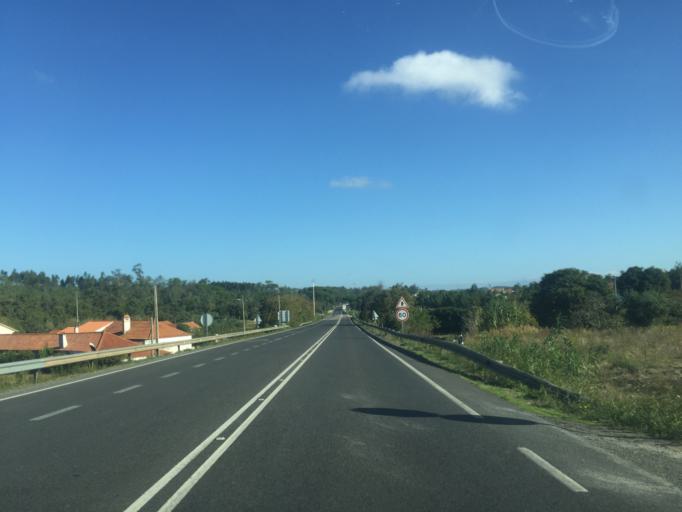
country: PT
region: Leiria
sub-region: Alcobaca
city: Aljubarrota
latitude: 39.5795
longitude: -8.8729
